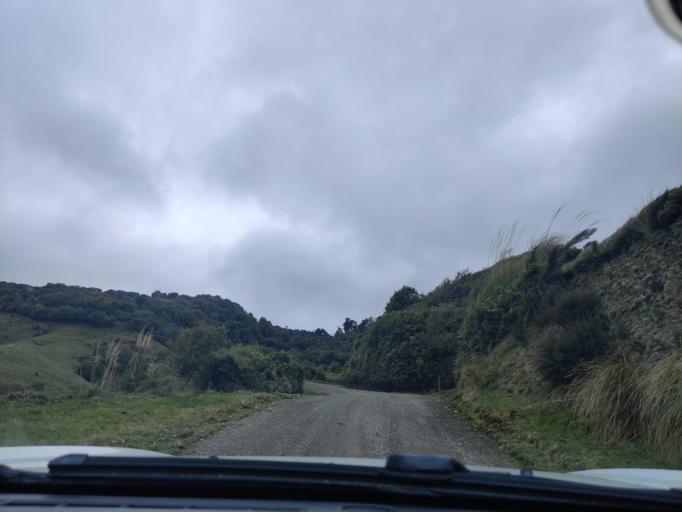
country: NZ
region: Manawatu-Wanganui
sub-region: Palmerston North City
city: Palmerston North
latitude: -40.2740
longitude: 175.8495
